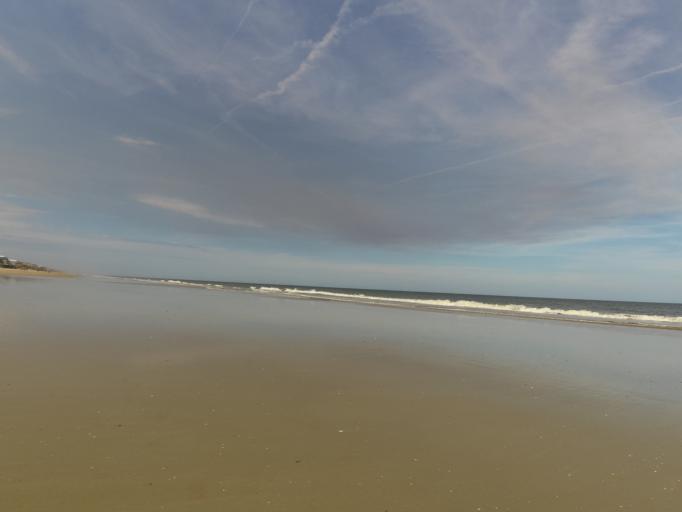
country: US
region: Florida
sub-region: Saint Johns County
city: Villano Beach
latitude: 29.9457
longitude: -81.3009
